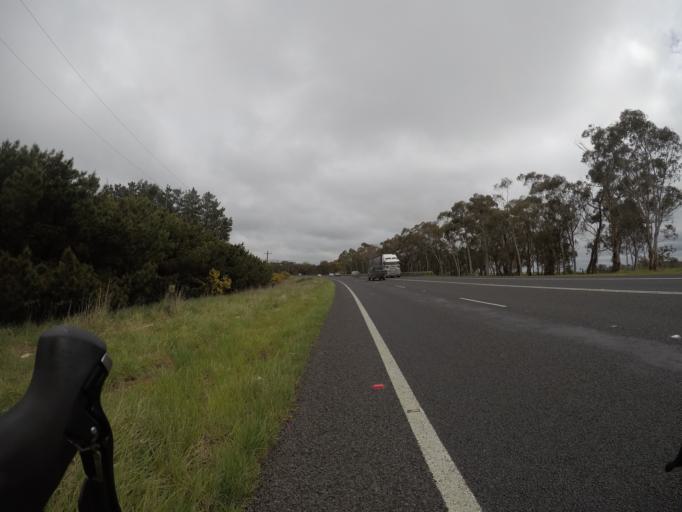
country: AU
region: New South Wales
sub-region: Lithgow
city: Portland
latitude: -33.4469
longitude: 150.0006
